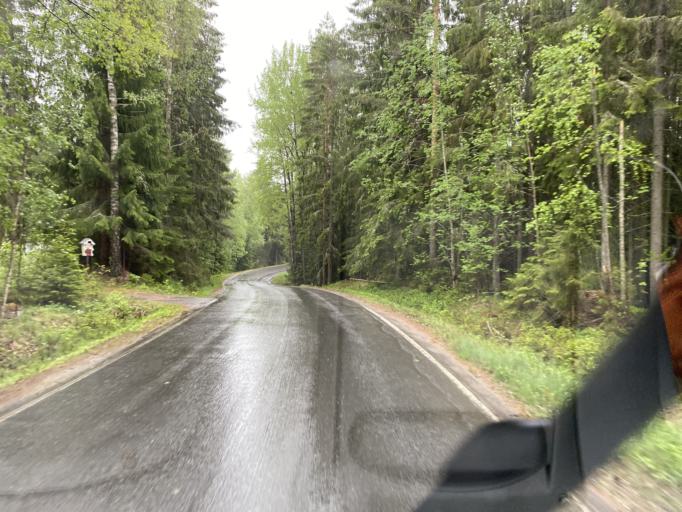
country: FI
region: Haeme
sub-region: Forssa
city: Humppila
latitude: 61.0758
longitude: 23.3107
